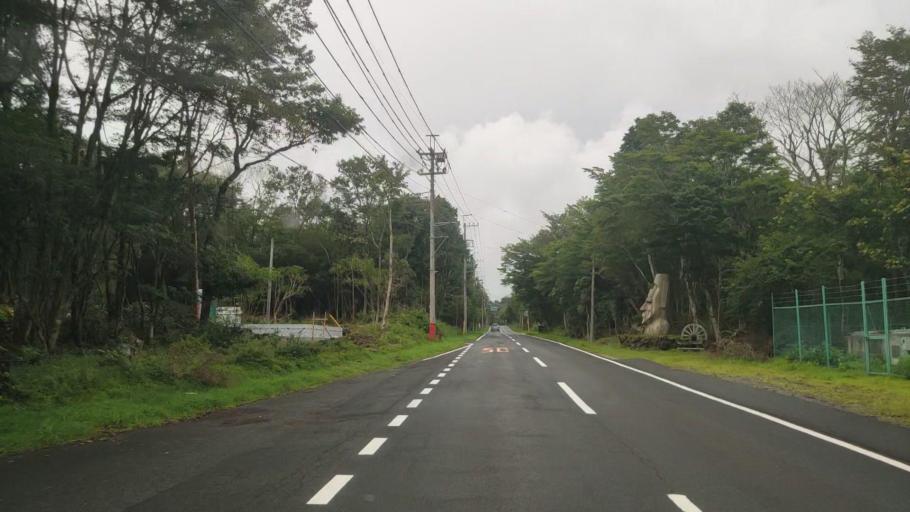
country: JP
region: Shizuoka
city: Gotemba
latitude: 35.2692
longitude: 138.8010
